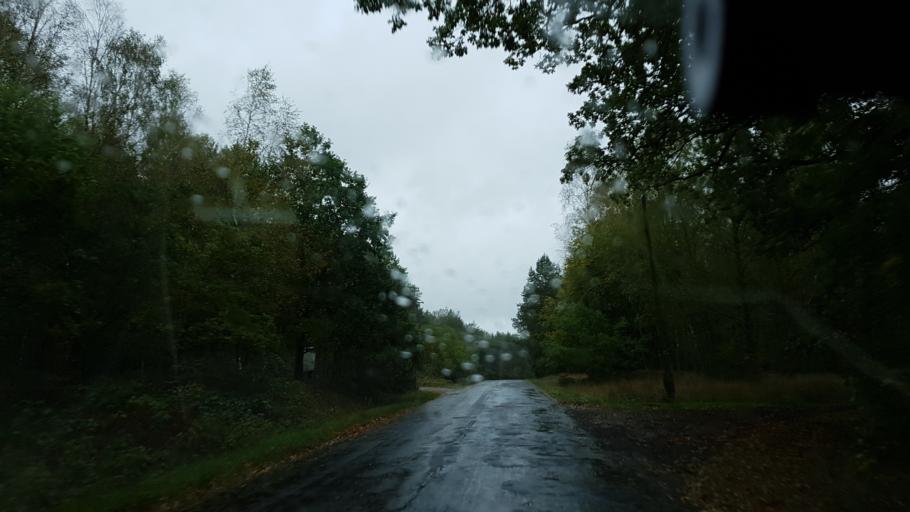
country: PL
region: West Pomeranian Voivodeship
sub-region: Powiat goleniowski
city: Stepnica
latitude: 53.6795
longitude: 14.7187
